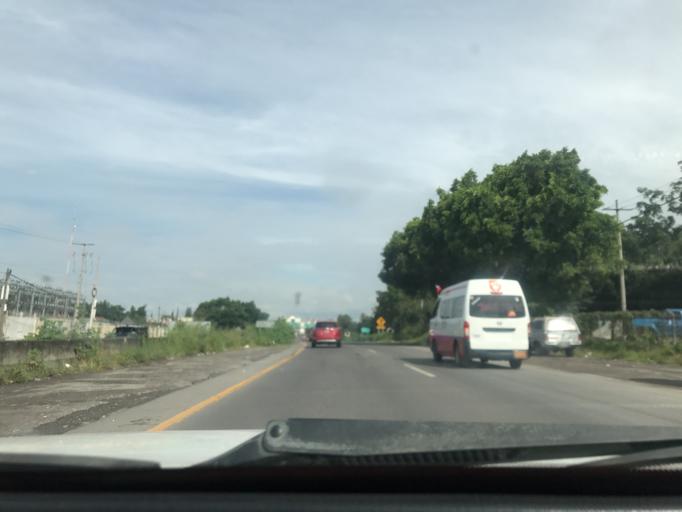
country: MX
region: Morelos
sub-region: Cuautla
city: Tierra Larga (Campo Nuevo)
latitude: 18.8460
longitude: -98.9305
